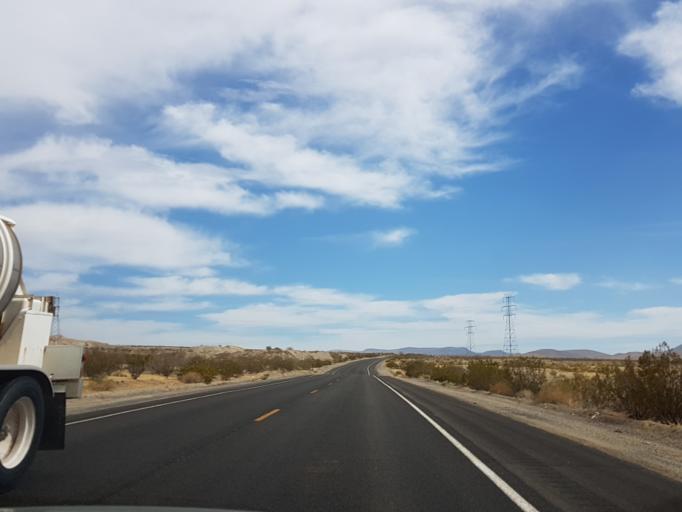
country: US
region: California
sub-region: Kern County
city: Ridgecrest
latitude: 35.4264
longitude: -117.7030
